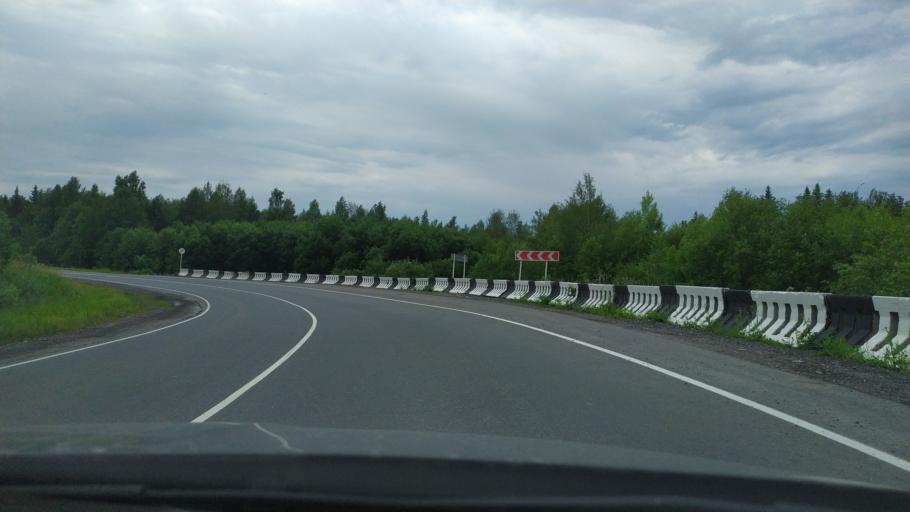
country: RU
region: Perm
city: Chusovoy
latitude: 58.4088
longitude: 57.8738
